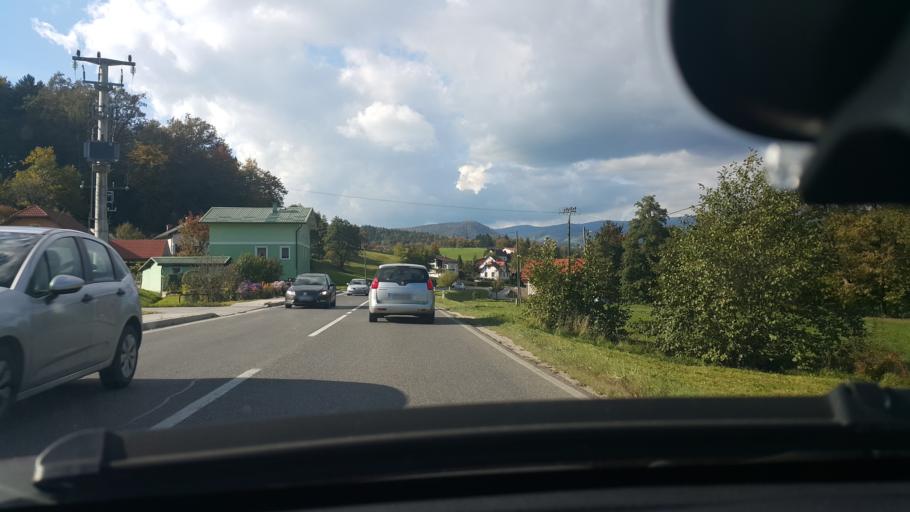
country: SI
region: Slovenska Konjice
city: Slovenske Konjice
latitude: 46.3493
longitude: 15.4036
